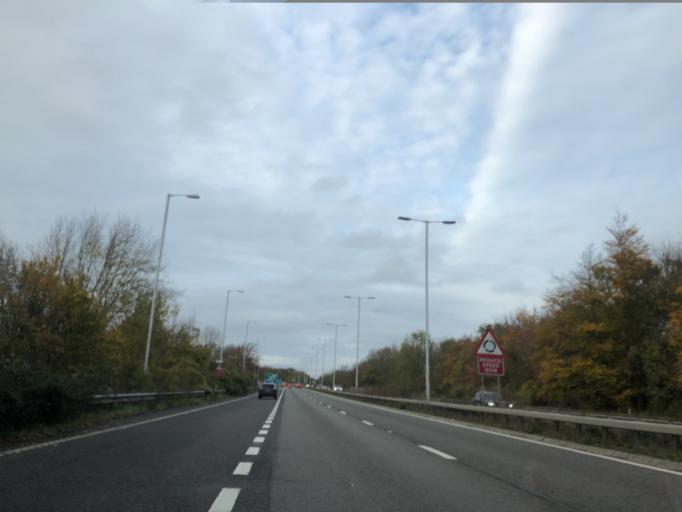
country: GB
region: England
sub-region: Buckinghamshire
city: High Wycombe
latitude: 51.6071
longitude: -0.7659
